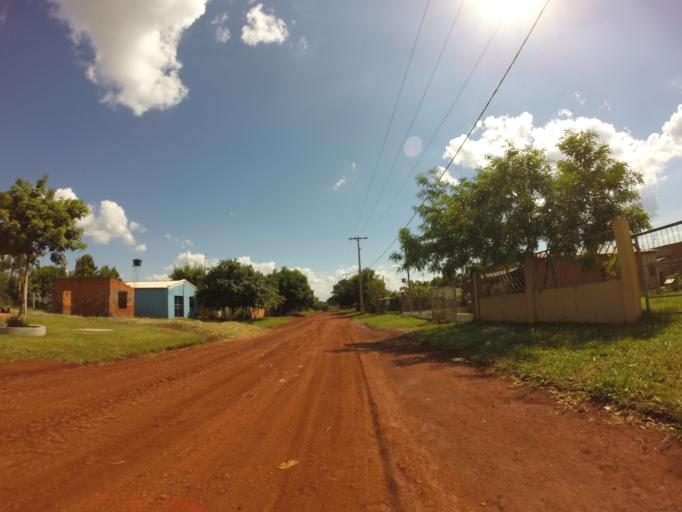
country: PY
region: Alto Parana
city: Ciudad del Este
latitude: -25.3770
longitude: -54.6584
